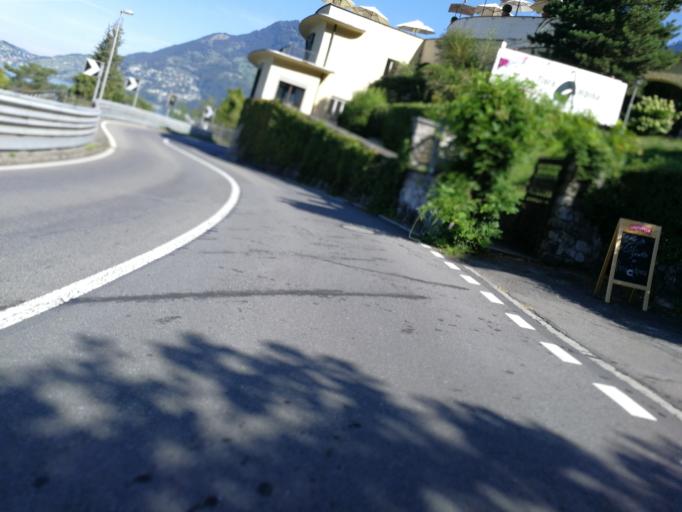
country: CH
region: Lucerne
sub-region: Lucerne-Land District
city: Vitznau
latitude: 46.9984
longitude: 8.4780
